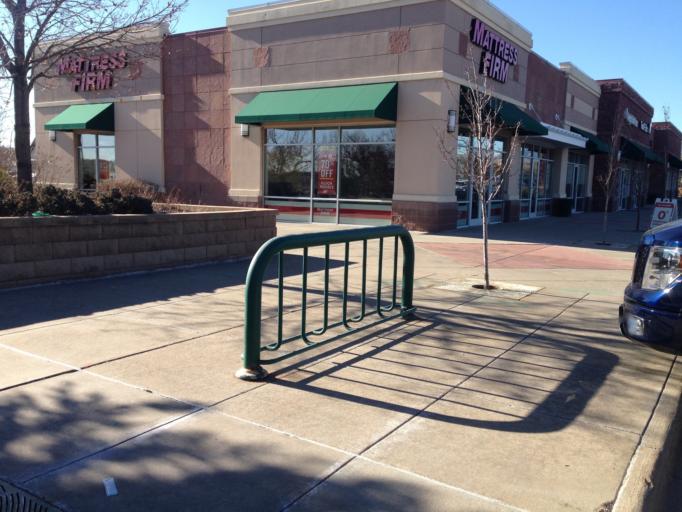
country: US
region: Colorado
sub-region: Boulder County
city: Superior
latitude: 39.9557
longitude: -105.1675
